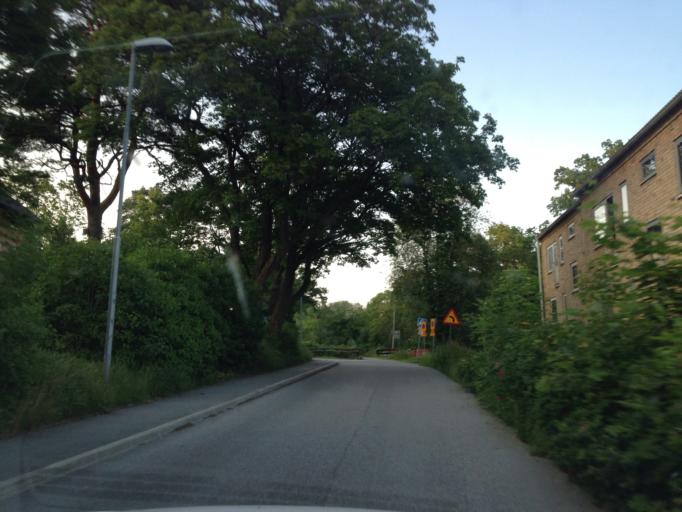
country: SE
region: Stockholm
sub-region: Varmdo Kommun
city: Gustavsberg
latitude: 59.3217
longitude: 18.3905
